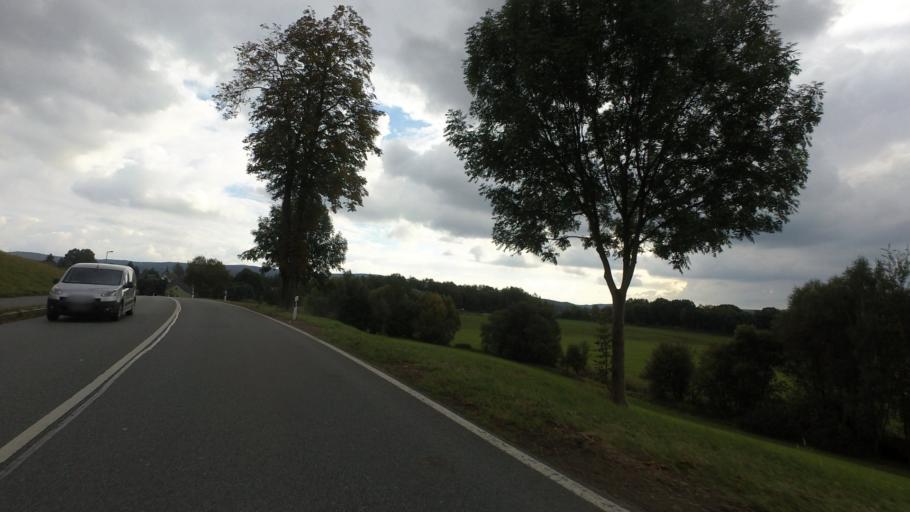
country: DE
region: Saxony
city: Grosspostwitz
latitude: 51.1089
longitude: 14.4568
